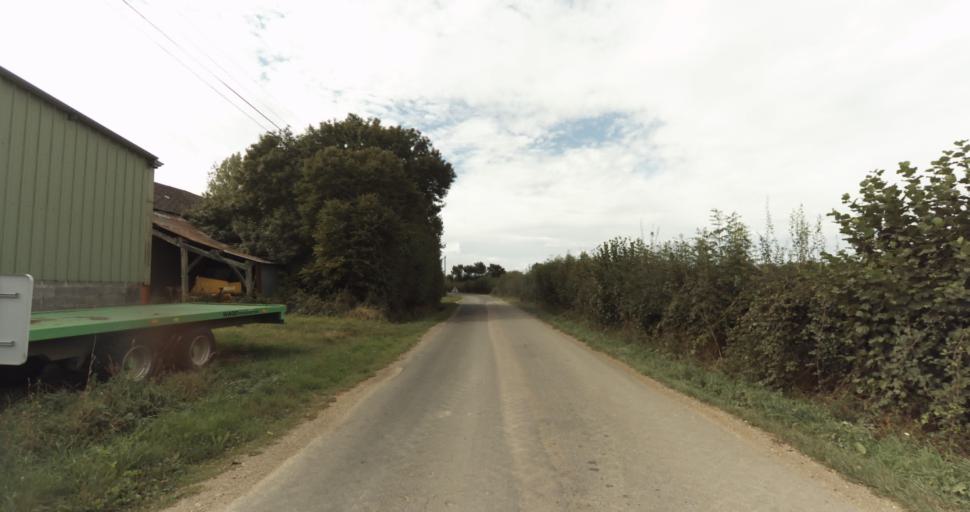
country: FR
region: Lower Normandy
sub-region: Departement du Calvados
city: La Vespiere
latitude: 48.9457
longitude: 0.3510
